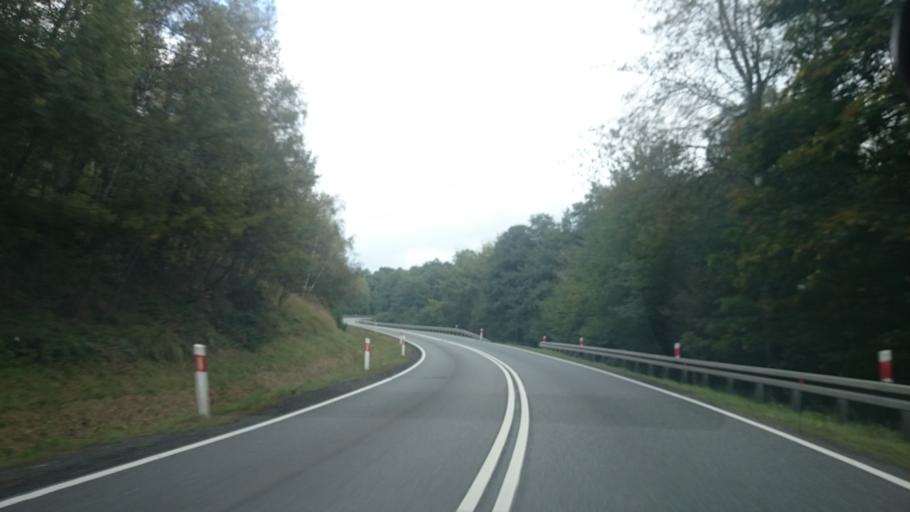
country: PL
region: Lower Silesian Voivodeship
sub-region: Powiat zabkowicki
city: Zloty Stok
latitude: 50.4355
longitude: 16.7998
